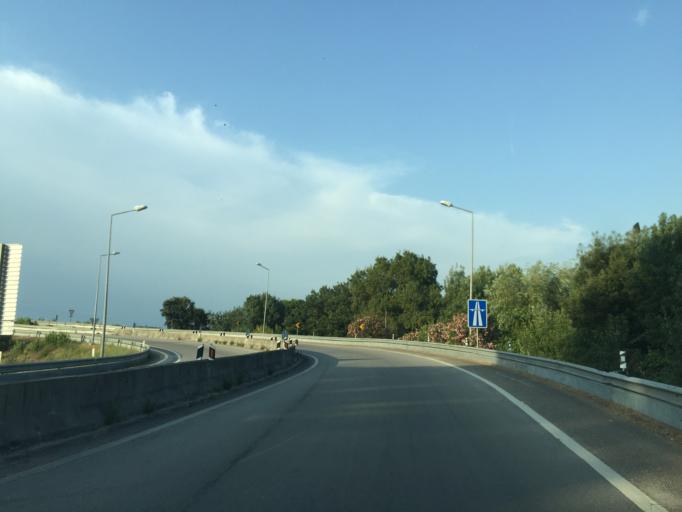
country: PT
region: Santarem
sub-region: Tomar
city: Tomar
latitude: 39.5511
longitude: -8.3892
